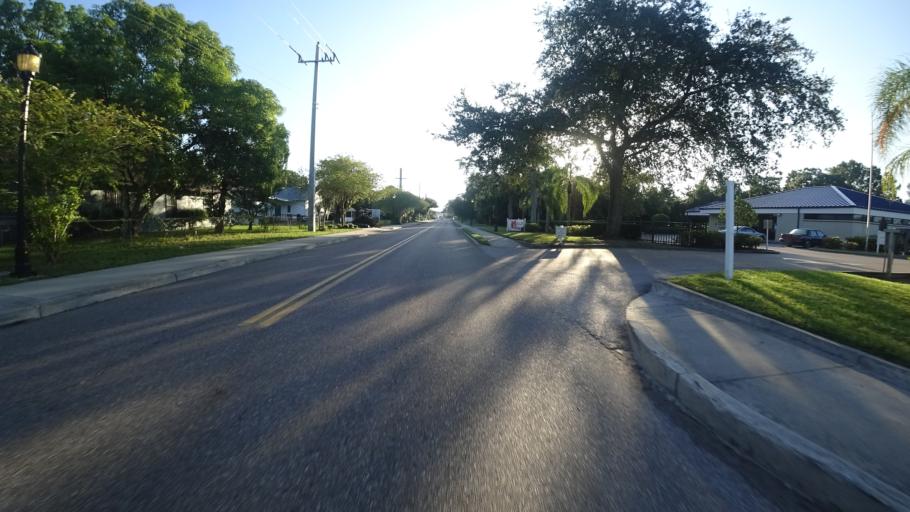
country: US
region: Florida
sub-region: Manatee County
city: West Samoset
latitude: 27.4880
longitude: -82.5584
